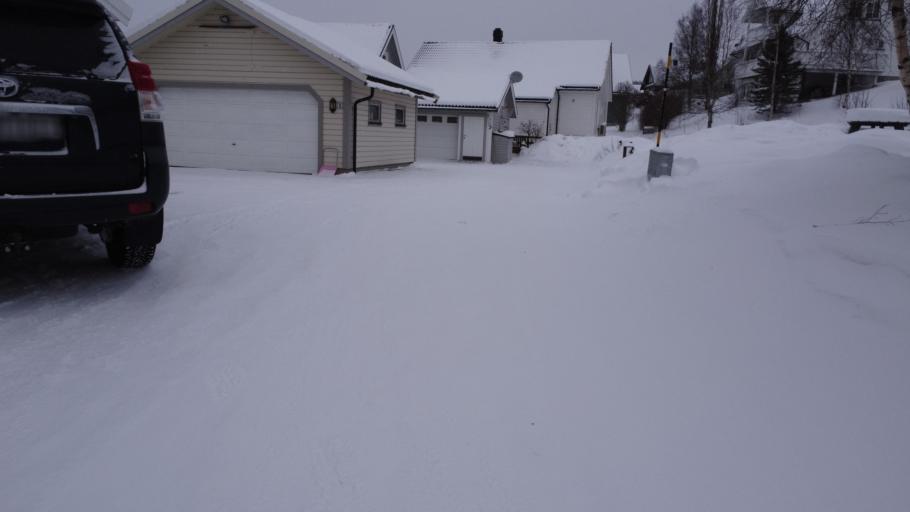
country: NO
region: Nordland
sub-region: Rana
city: Mo i Rana
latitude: 66.3306
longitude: 14.1533
